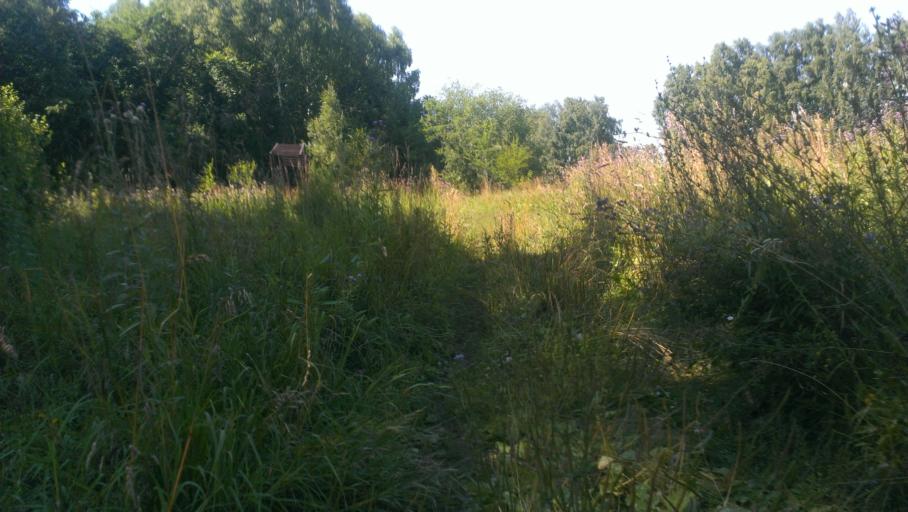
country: RU
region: Altai Krai
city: Nauchnyy Gorodok
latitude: 53.4236
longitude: 83.5102
